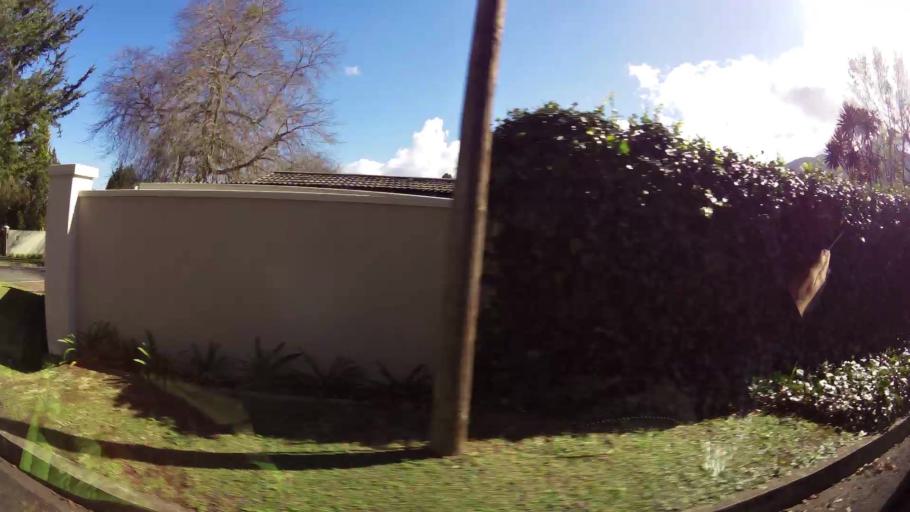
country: ZA
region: Western Cape
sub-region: Eden District Municipality
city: George
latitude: -33.9479
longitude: 22.4605
